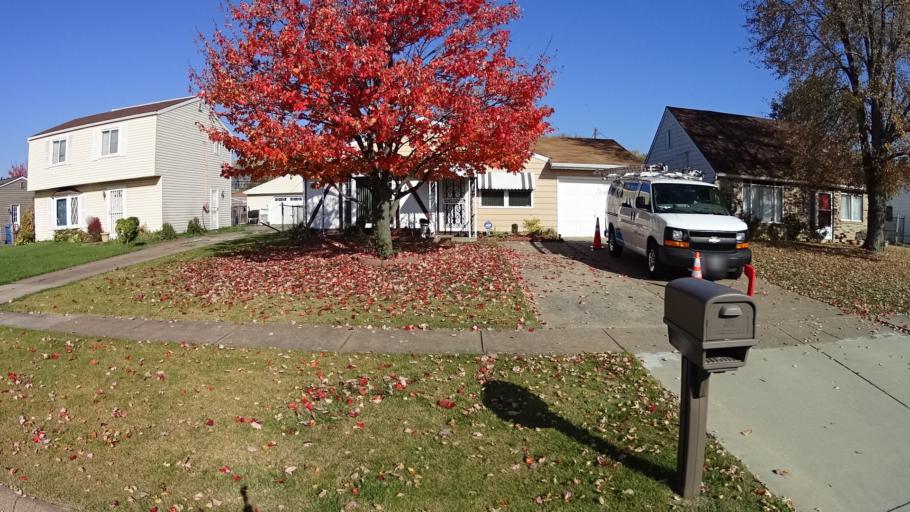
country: US
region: Ohio
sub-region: Lorain County
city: Lorain
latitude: 41.4687
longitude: -82.1489
